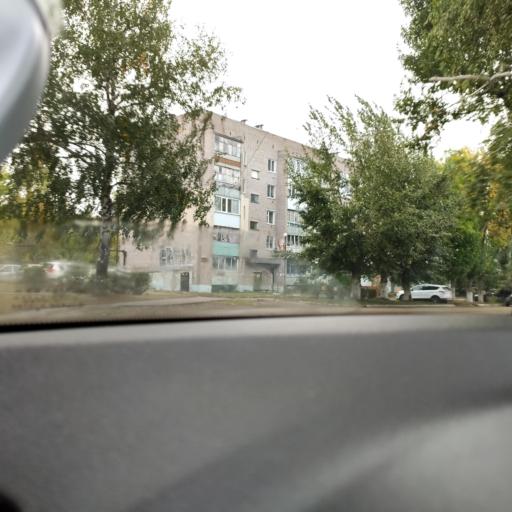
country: RU
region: Samara
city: Novosemeykino
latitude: 53.3709
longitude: 50.3622
